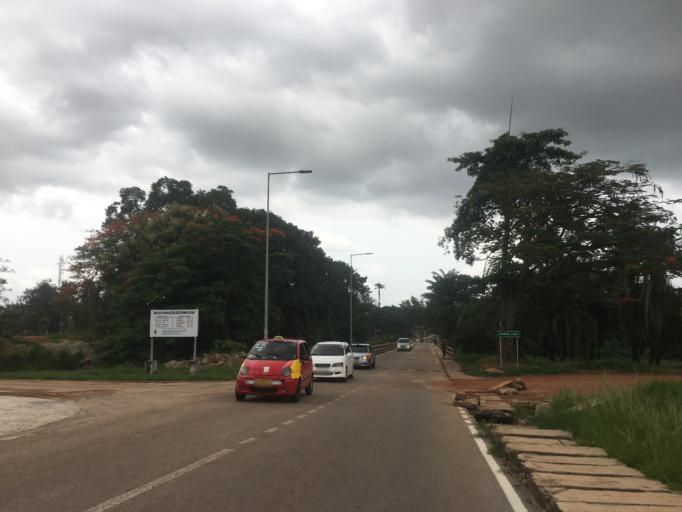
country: GH
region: Ashanti
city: Kumasi
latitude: 6.6843
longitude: -1.5725
